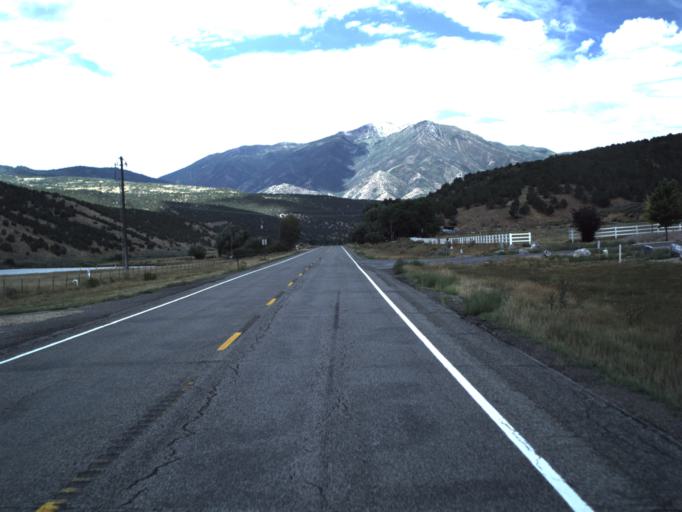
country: US
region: Utah
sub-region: Utah County
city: Woodland Hills
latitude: 39.8734
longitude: -111.5376
